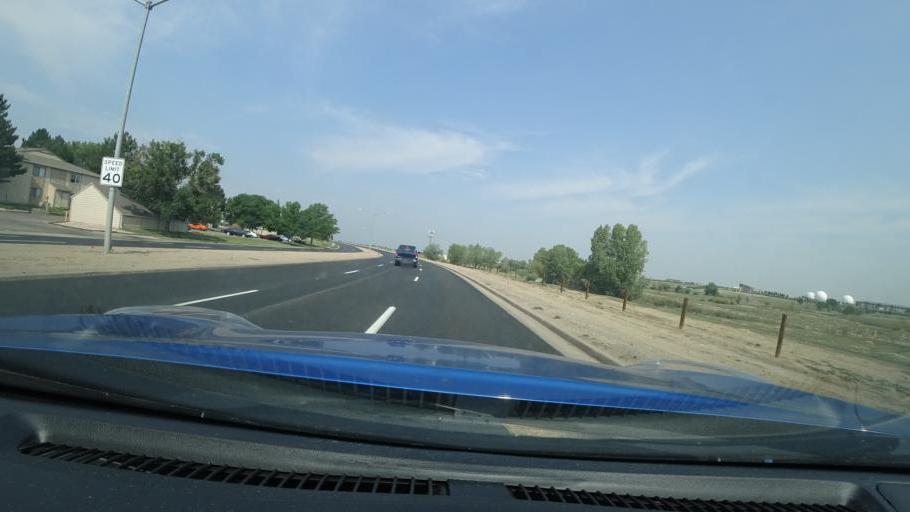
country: US
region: Colorado
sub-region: Adams County
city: Aurora
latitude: 39.7043
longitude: -104.7771
